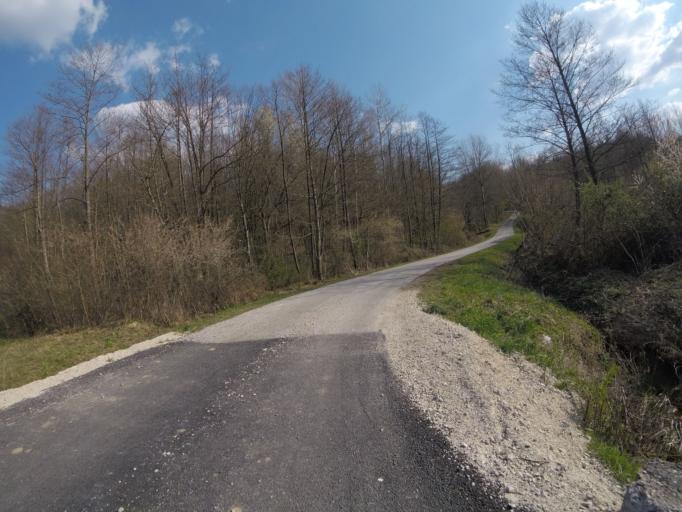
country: HR
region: Sisacko-Moslavacka
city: Glina
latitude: 45.5034
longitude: 16.0084
